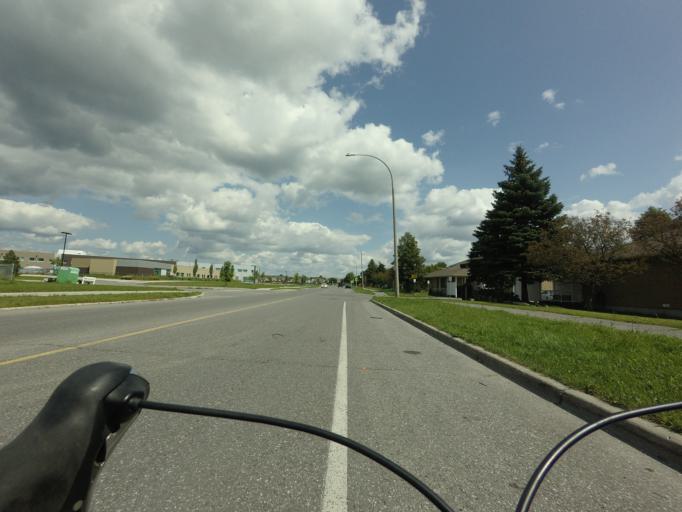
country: CA
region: Ontario
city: Bells Corners
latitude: 45.2773
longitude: -75.8602
